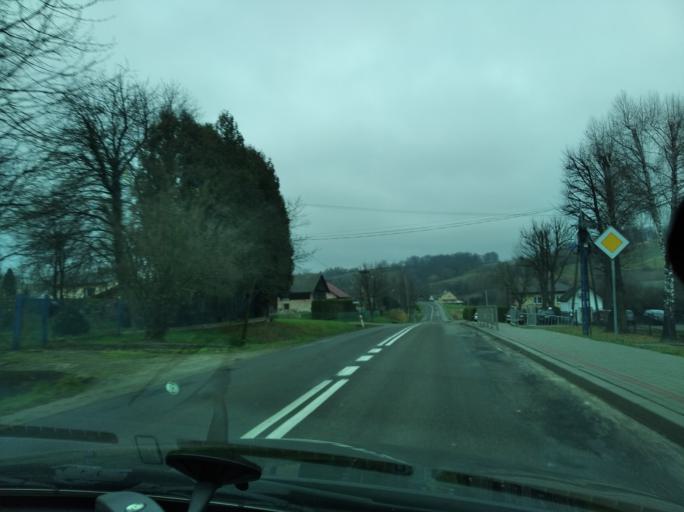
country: PL
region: Subcarpathian Voivodeship
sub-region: Powiat przeworski
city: Jawornik Polski
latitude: 49.8748
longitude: 22.2456
